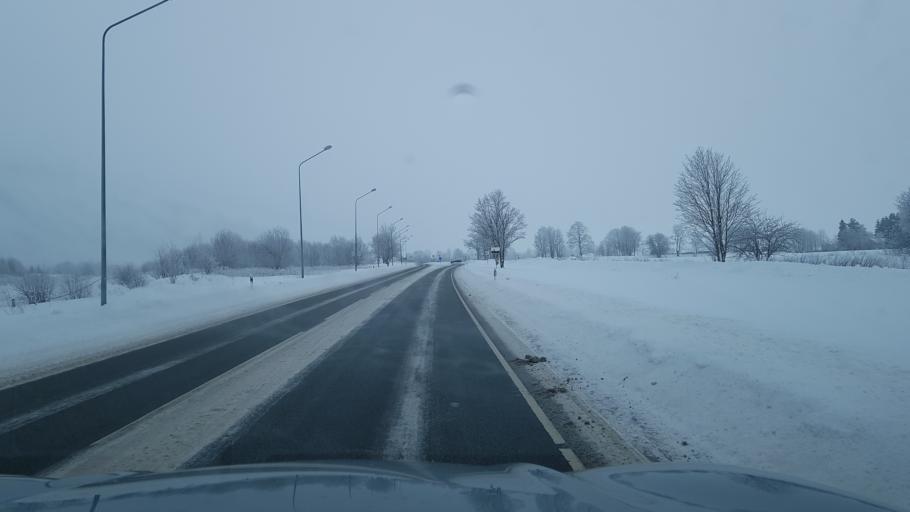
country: EE
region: Ida-Virumaa
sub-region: Johvi vald
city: Johvi
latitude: 59.3408
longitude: 27.4034
